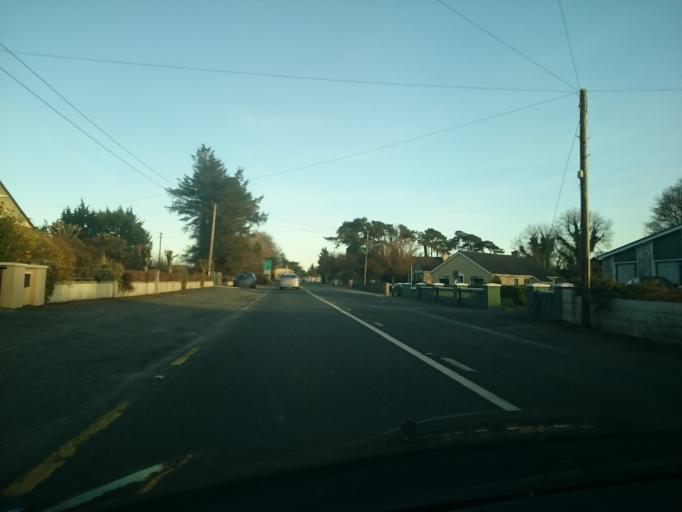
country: IE
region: Connaught
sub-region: Maigh Eo
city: Claremorris
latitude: 53.7391
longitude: -9.0105
